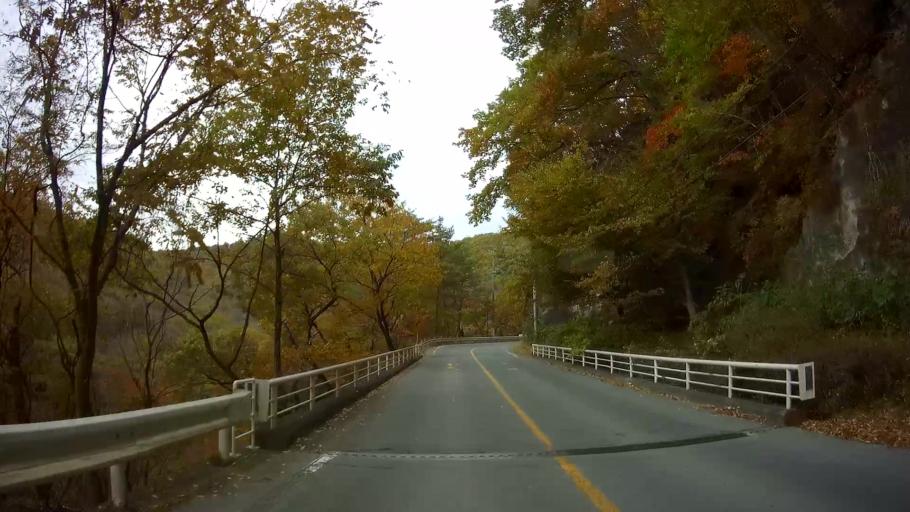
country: JP
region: Gunma
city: Nakanojomachi
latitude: 36.5577
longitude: 138.6404
